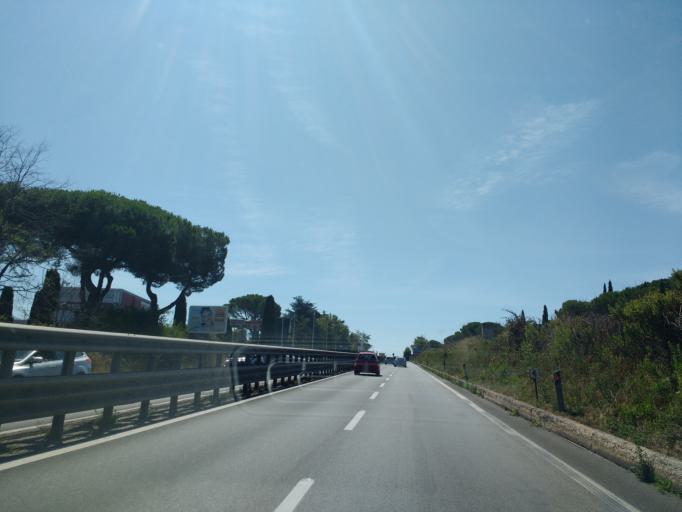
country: IT
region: Latium
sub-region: Citta metropolitana di Roma Capitale
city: Marino
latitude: 41.7705
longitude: 12.6128
